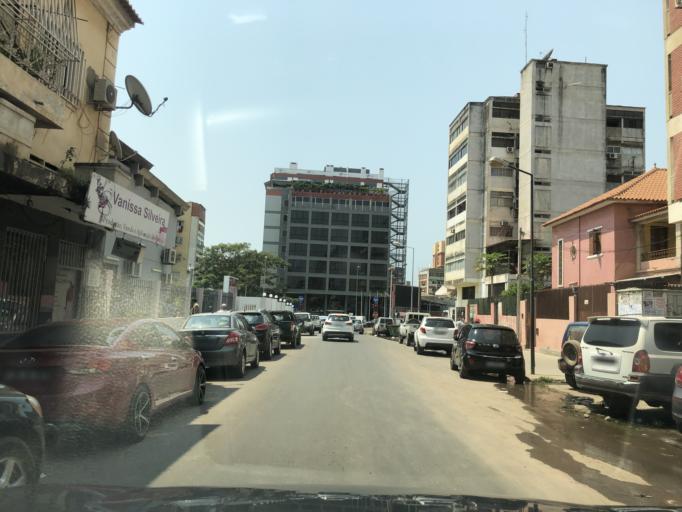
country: AO
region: Luanda
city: Luanda
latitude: -8.8185
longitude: 13.2453
